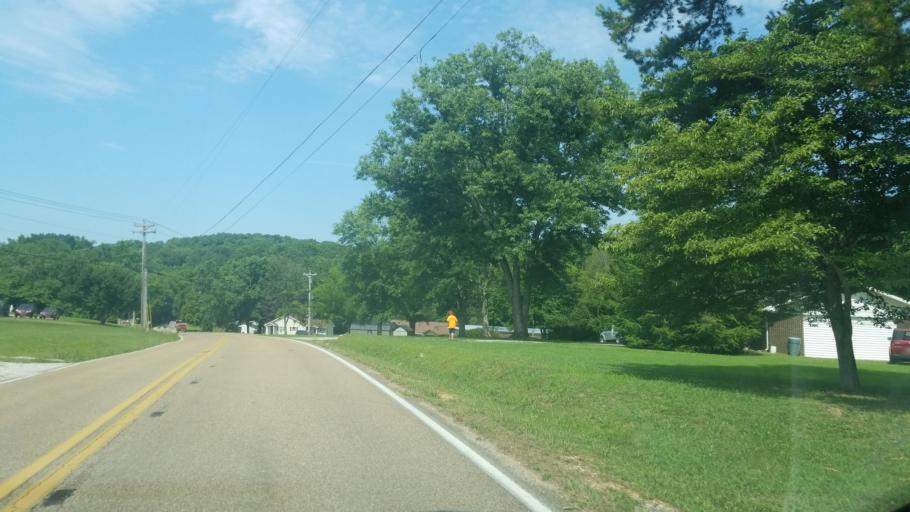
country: US
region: Tennessee
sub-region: Hamilton County
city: Lakesite
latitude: 35.1682
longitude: -85.0630
